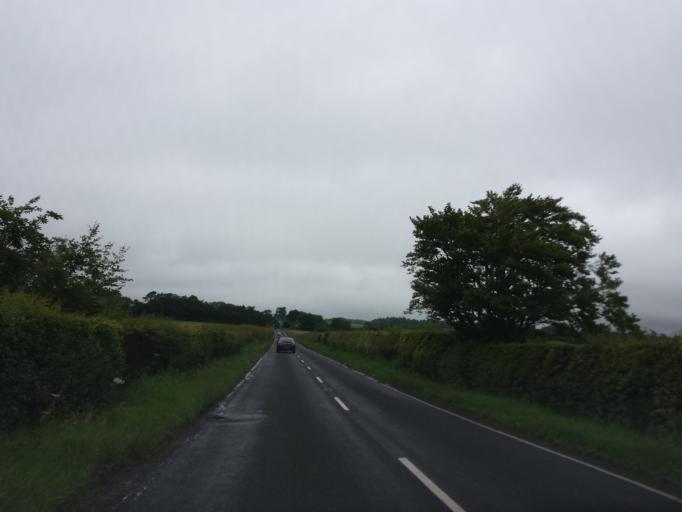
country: GB
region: Scotland
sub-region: Fife
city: Lundin Links
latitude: 56.2397
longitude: -2.8988
